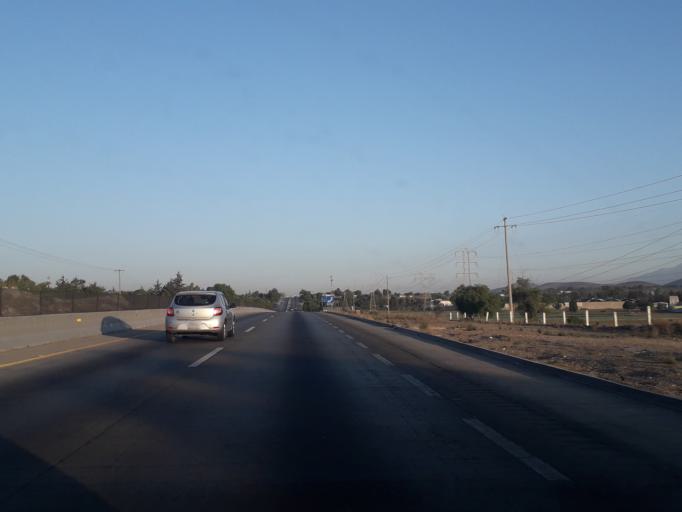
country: MX
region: Puebla
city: Acatzingo de Hidalgo
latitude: 18.9728
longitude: -97.7984
